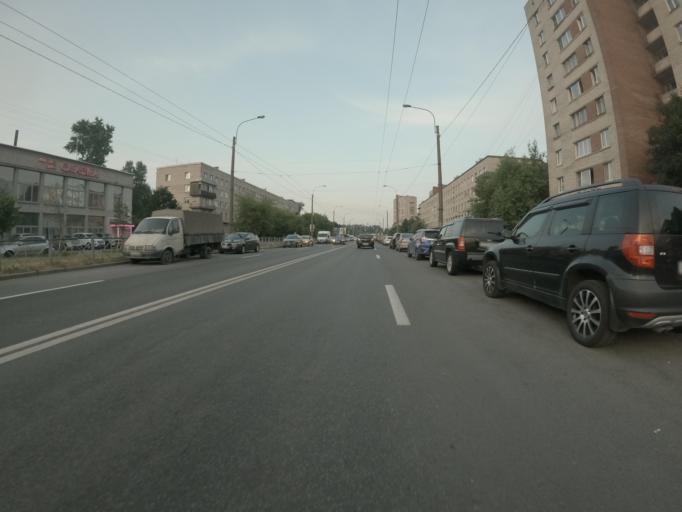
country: RU
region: Leningrad
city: Kalininskiy
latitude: 59.9703
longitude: 30.4038
